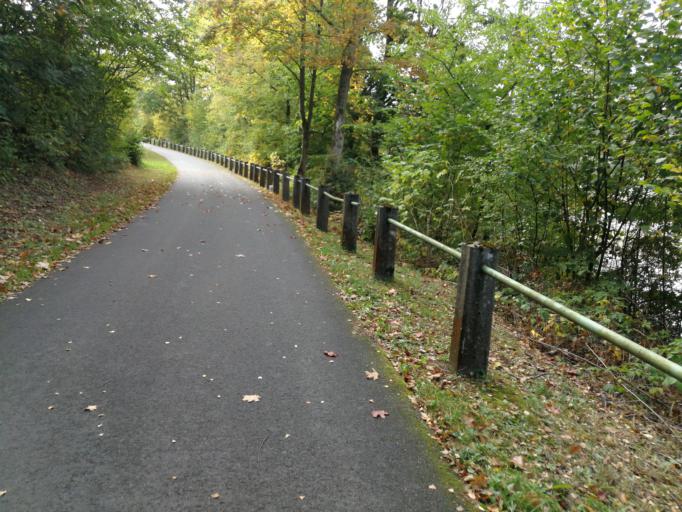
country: DE
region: North Rhine-Westphalia
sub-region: Regierungsbezirk Arnsberg
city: Meschede
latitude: 51.3105
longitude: 8.2617
